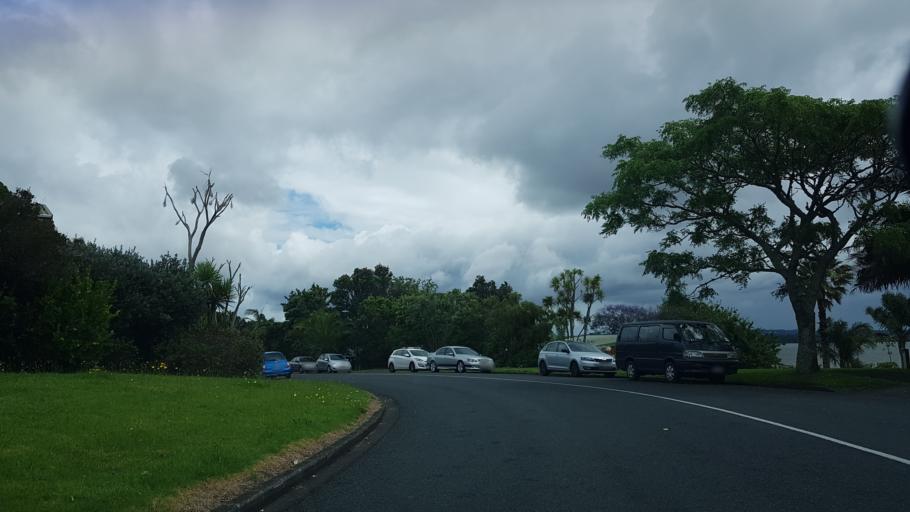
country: NZ
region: Auckland
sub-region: Auckland
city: Rosebank
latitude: -36.8311
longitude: 174.6580
